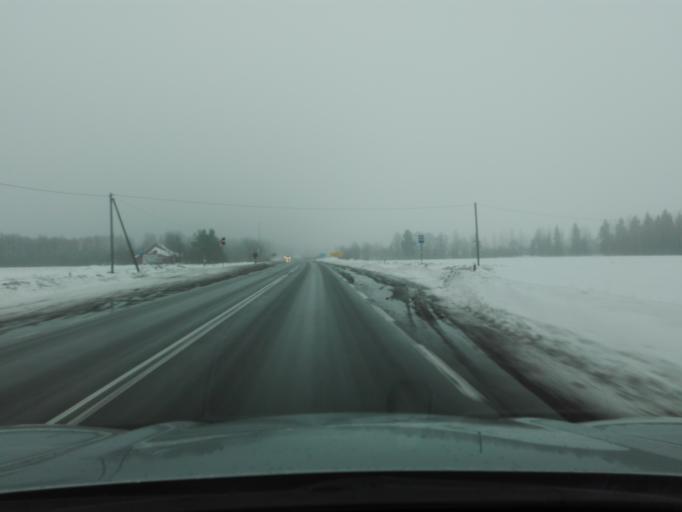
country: EE
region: Raplamaa
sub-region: Kohila vald
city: Kohila
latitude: 59.2008
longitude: 24.7831
